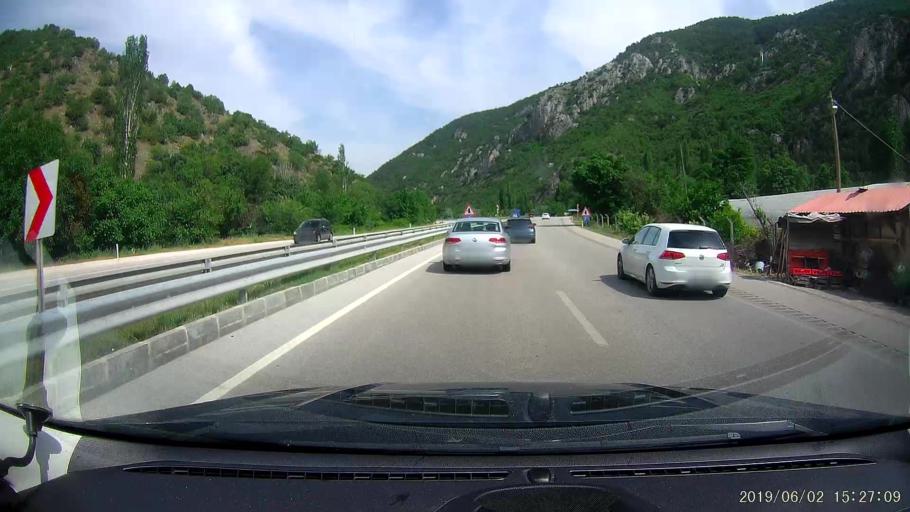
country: TR
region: Amasya
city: Saraycik
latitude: 40.9854
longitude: 35.0527
